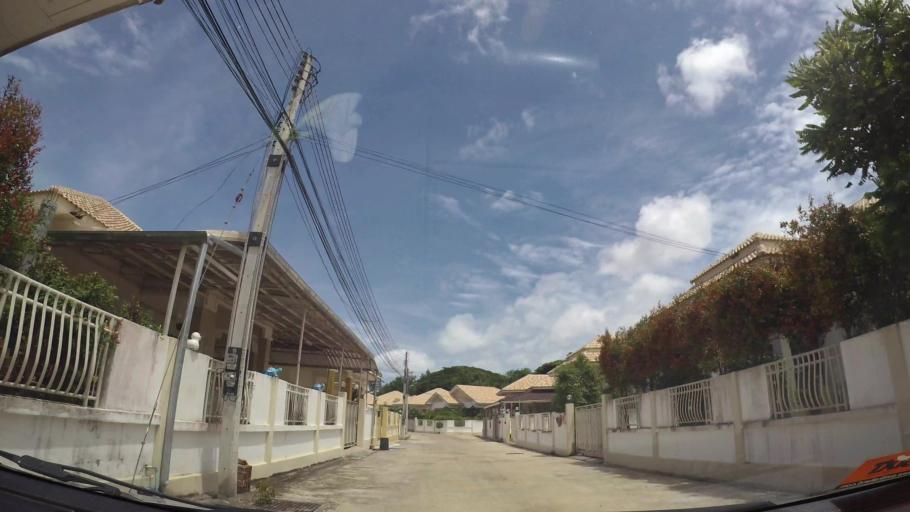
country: TH
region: Chon Buri
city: Sattahip
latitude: 12.7040
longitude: 100.8855
